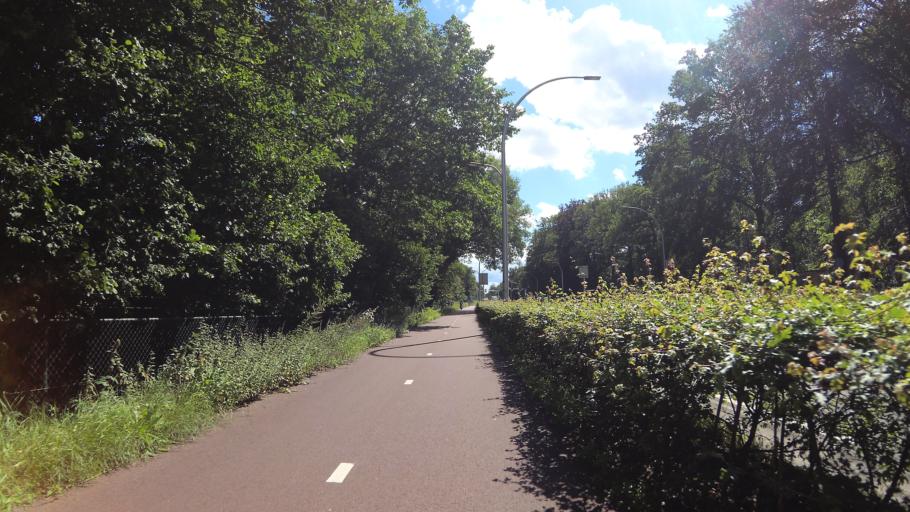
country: NL
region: North Brabant
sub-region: Gemeente Goirle
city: Goirle
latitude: 51.5619
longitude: 5.0156
